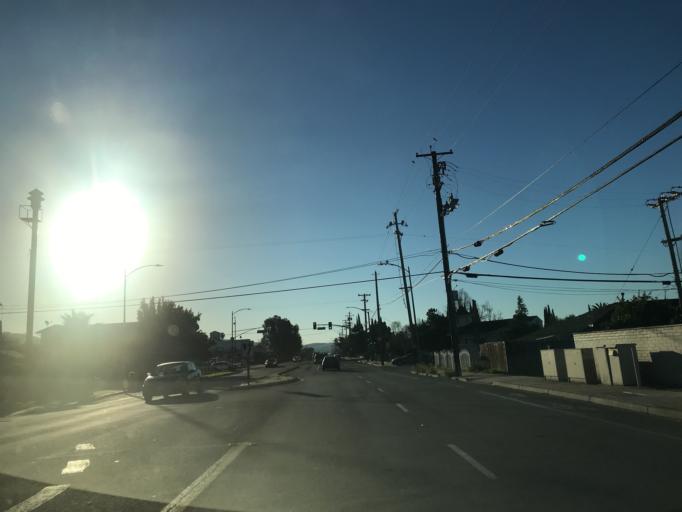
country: US
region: California
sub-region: Santa Clara County
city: Alum Rock
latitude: 37.3517
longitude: -121.8151
